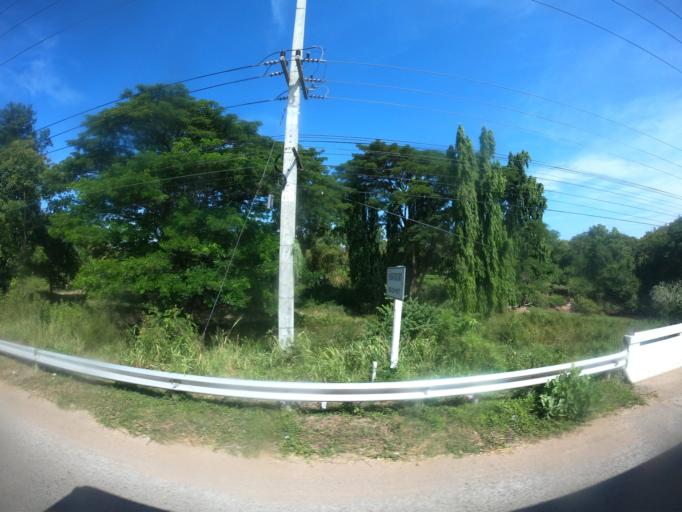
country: TH
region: Khon Kaen
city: Khon Kaen
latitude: 16.4469
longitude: 102.9548
